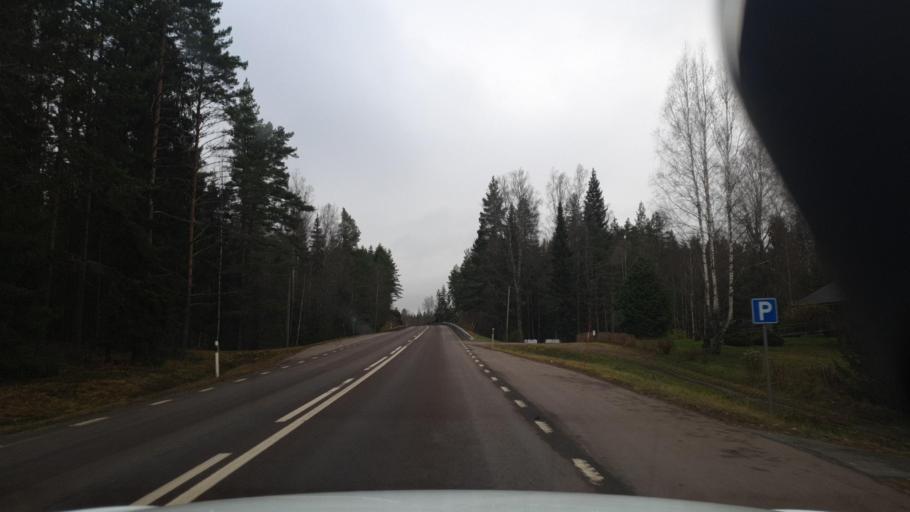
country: SE
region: Vaermland
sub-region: Karlstads Kommun
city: Edsvalla
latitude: 59.5918
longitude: 13.0097
